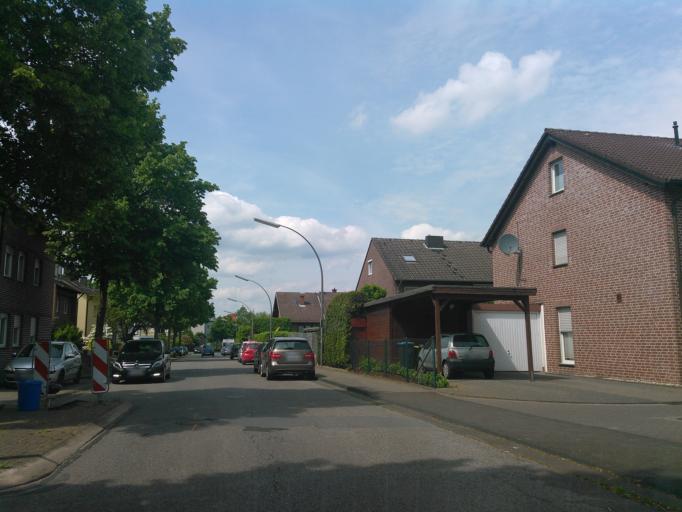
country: DE
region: North Rhine-Westphalia
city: Marl
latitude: 51.6537
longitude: 7.0713
